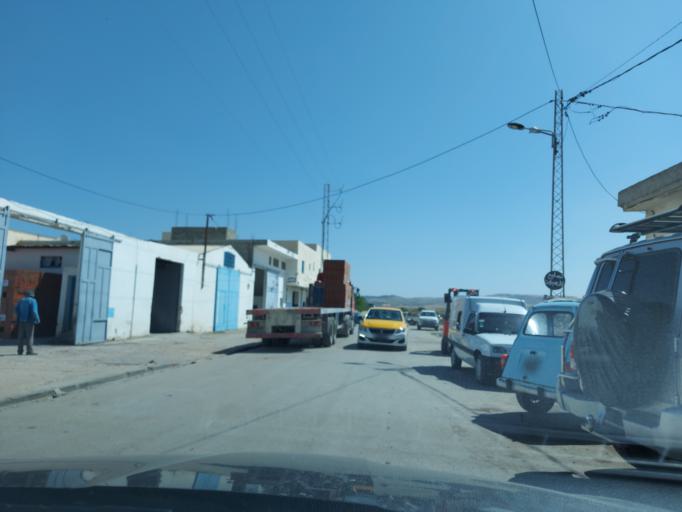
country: TN
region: Silyanah
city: Siliana
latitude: 36.0908
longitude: 9.3771
